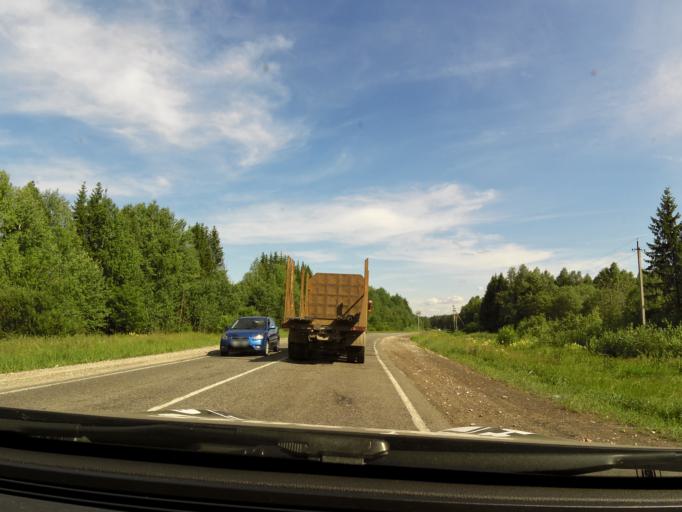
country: RU
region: Kirov
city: Belaya Kholunitsa
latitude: 58.8484
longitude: 50.7577
